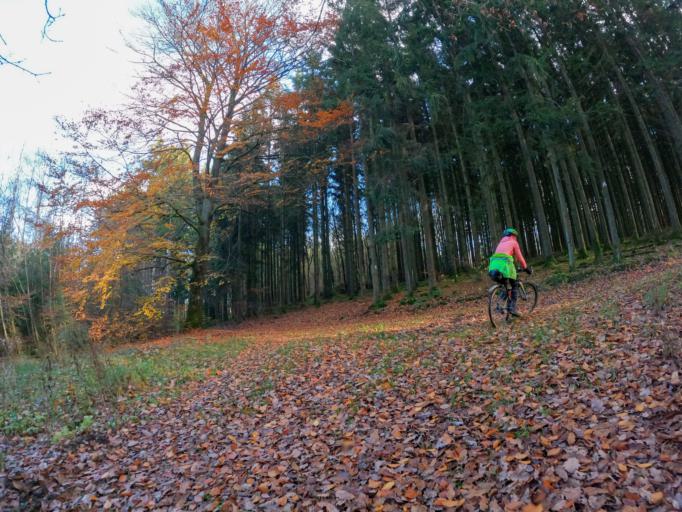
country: LU
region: Diekirch
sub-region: Canton de Wiltz
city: Winseler
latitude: 49.9879
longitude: 5.8421
